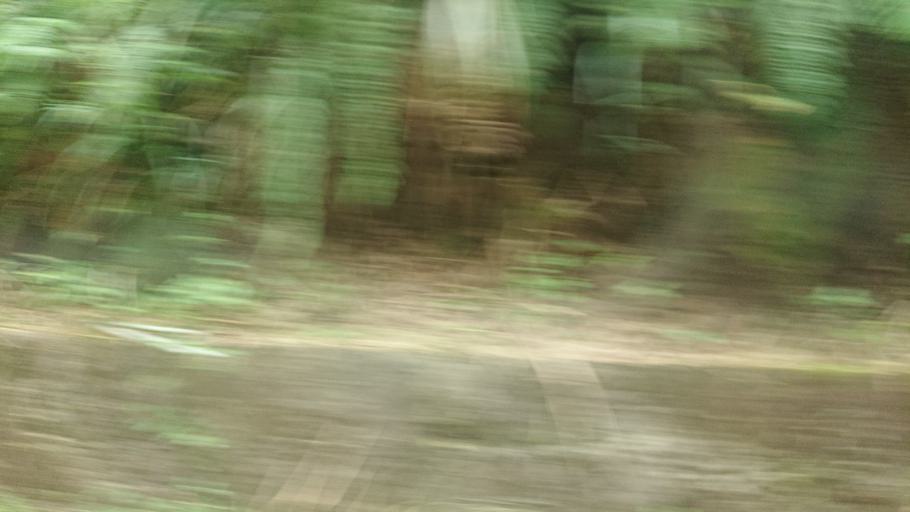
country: TW
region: Taiwan
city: Lugu
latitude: 23.6274
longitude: 120.7153
